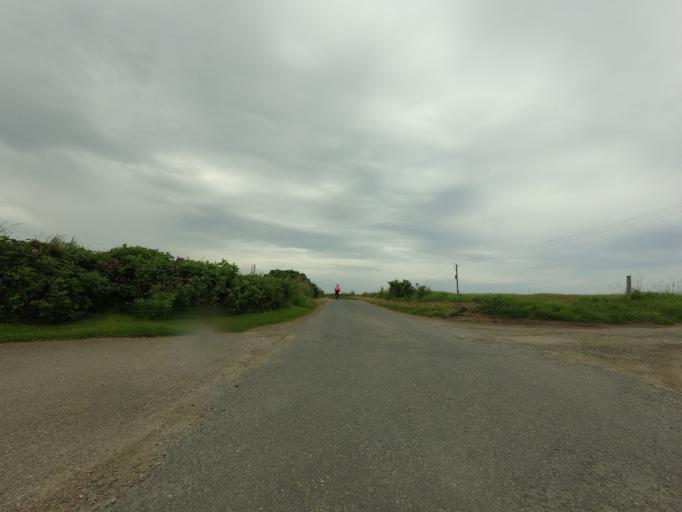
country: GB
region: Scotland
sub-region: Aberdeenshire
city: Portsoy
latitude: 57.6791
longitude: -2.6751
